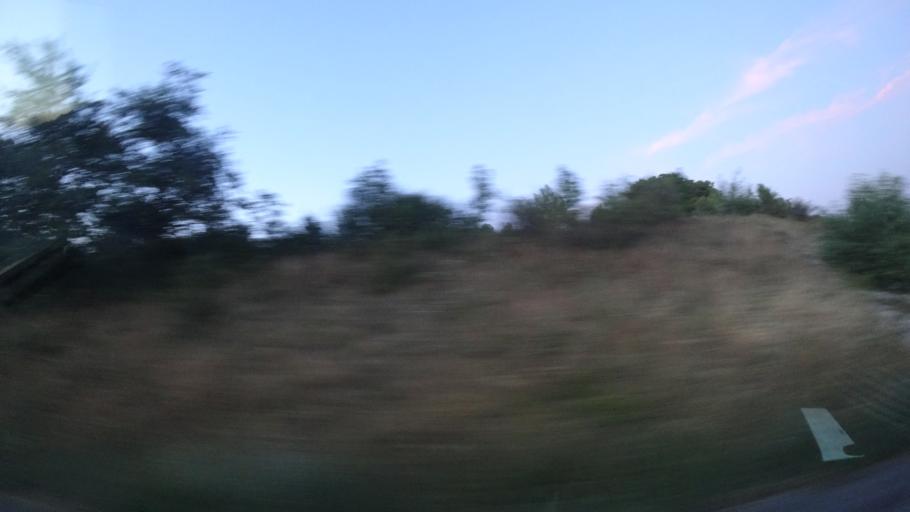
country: FR
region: Midi-Pyrenees
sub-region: Departement de l'Aveyron
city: Creissels
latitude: 44.1292
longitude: 3.0459
